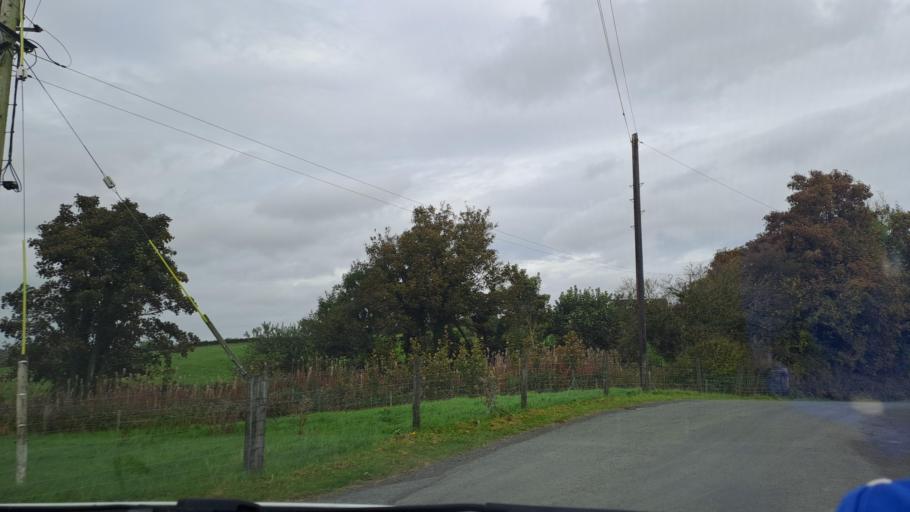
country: IE
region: Ulster
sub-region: An Cabhan
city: Kingscourt
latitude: 53.9387
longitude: -6.8196
